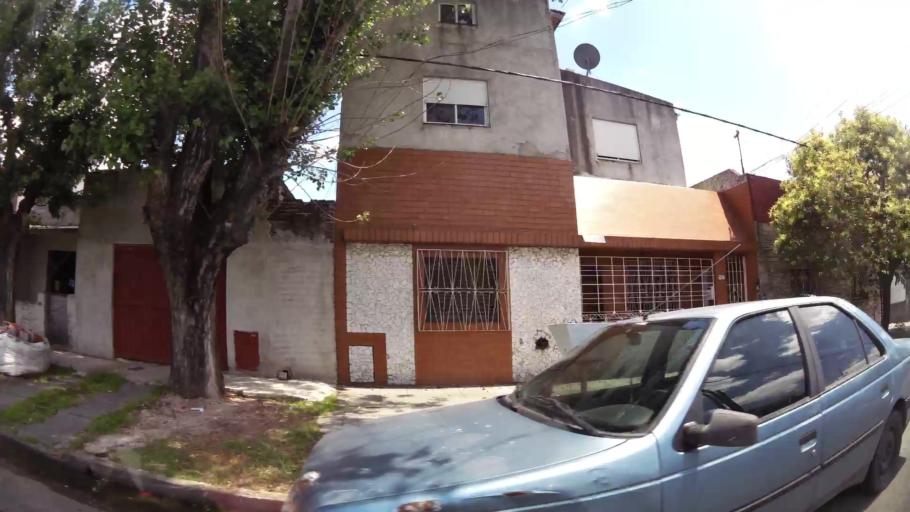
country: AR
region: Buenos Aires
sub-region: Partido de Lanus
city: Lanus
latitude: -34.7100
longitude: -58.4116
